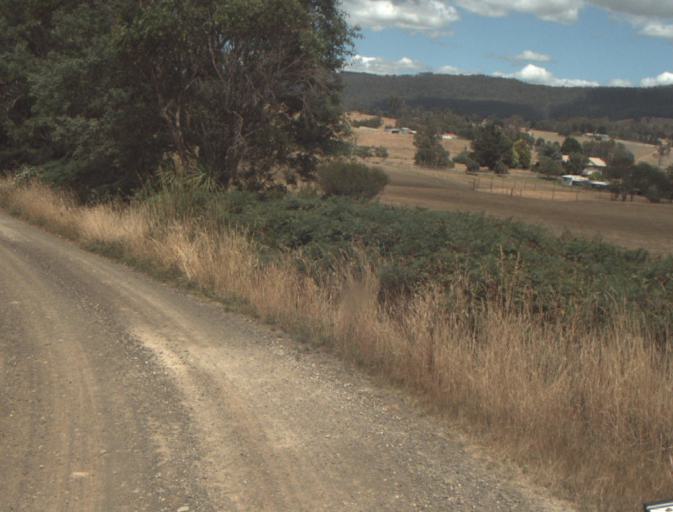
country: AU
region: Tasmania
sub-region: Launceston
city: Mayfield
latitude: -41.2085
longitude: 147.1501
